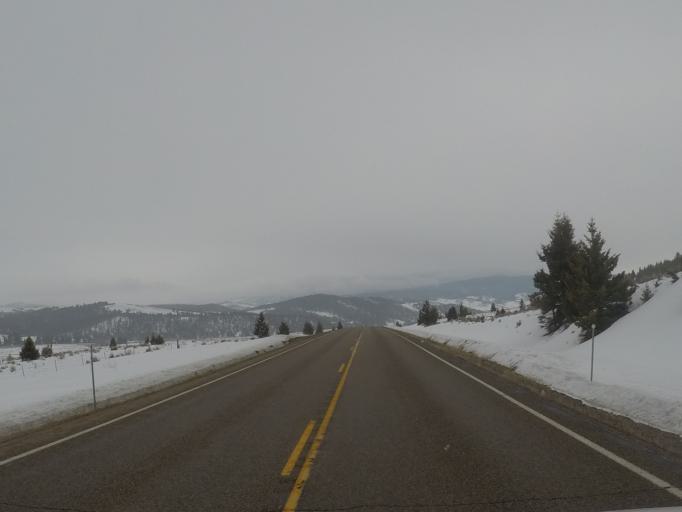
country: US
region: Montana
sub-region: Meagher County
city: White Sulphur Springs
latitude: 46.6360
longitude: -110.8561
